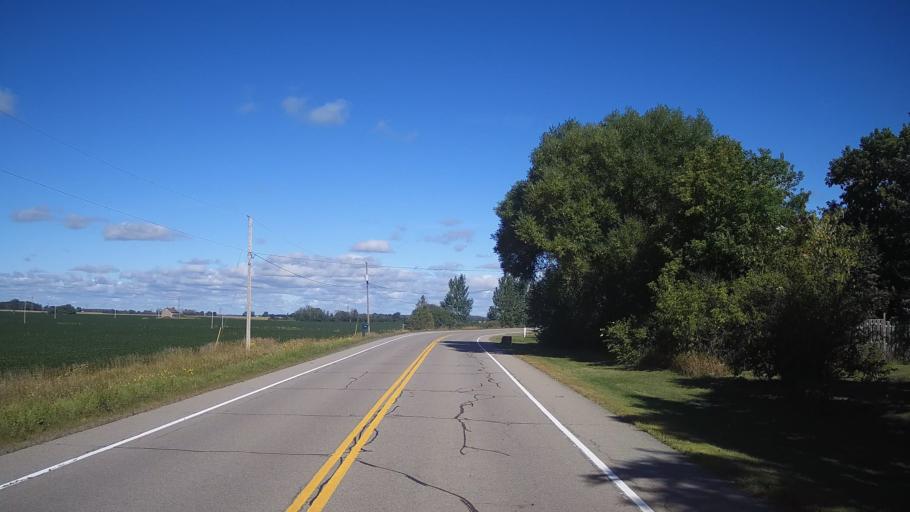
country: US
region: New York
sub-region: St. Lawrence County
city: Norfolk
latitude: 44.9569
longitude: -75.2817
